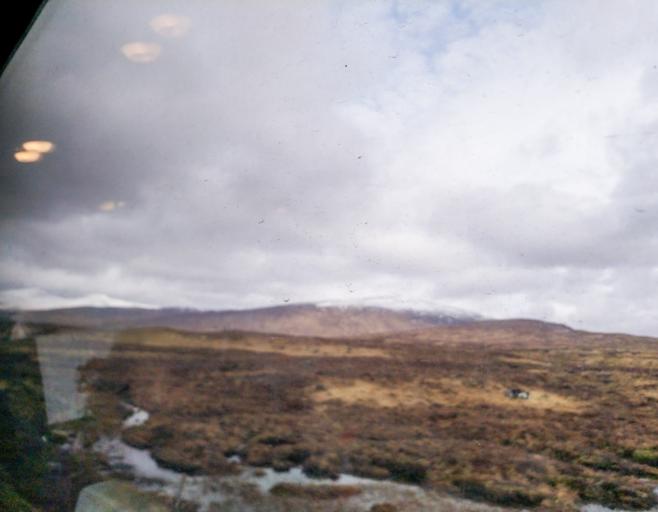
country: GB
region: Scotland
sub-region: Highland
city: Spean Bridge
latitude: 56.7375
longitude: -4.6576
